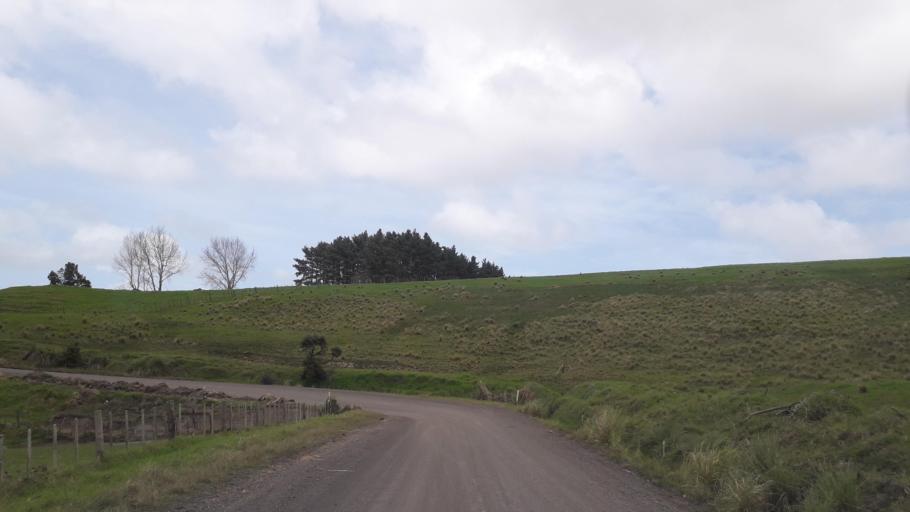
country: NZ
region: Northland
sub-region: Far North District
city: Kaitaia
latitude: -35.4088
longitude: 173.3638
